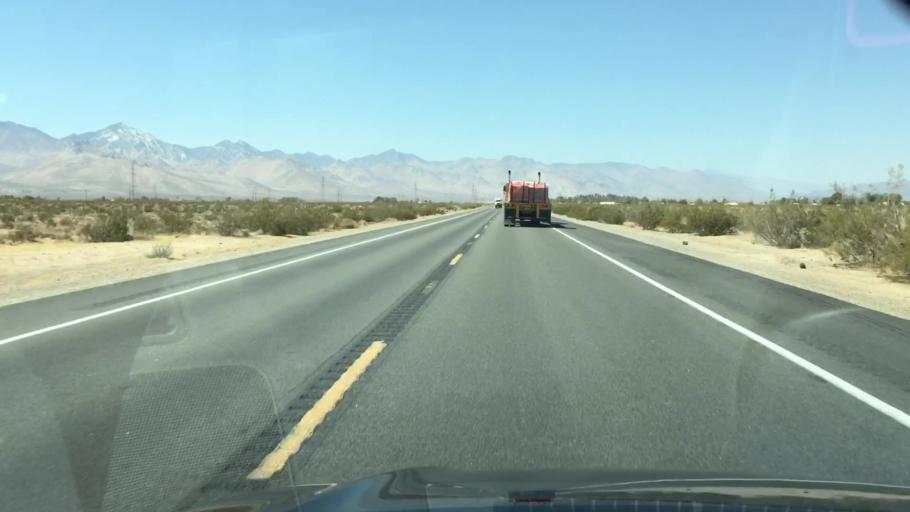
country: US
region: California
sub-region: Kern County
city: China Lake Acres
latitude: 35.6268
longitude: -117.7793
